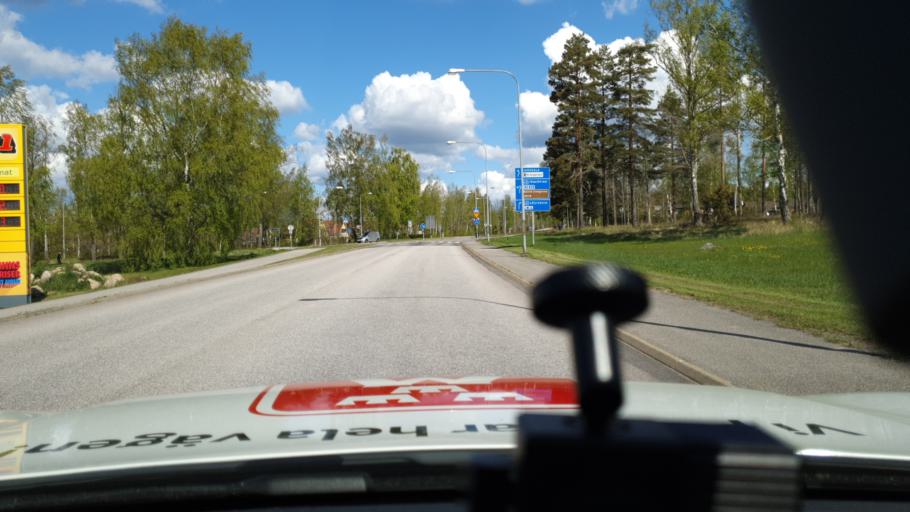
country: SE
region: Kalmar
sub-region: Vimmerby Kommun
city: Vimmerby
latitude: 57.6778
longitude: 15.8532
